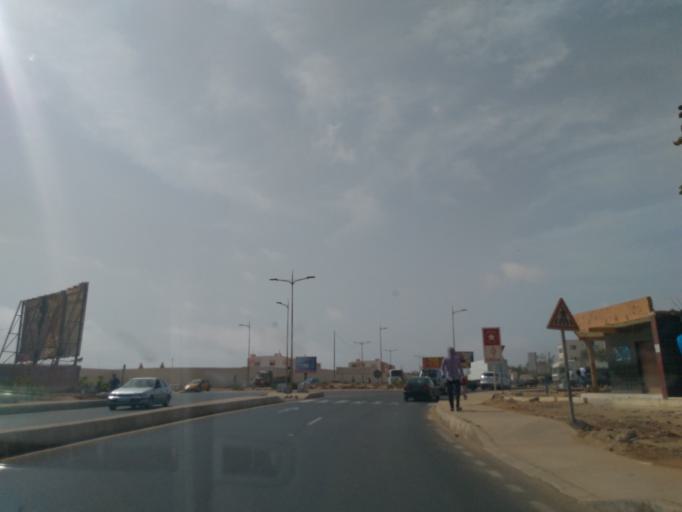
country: SN
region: Dakar
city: Mermoz Boabab
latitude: 14.7094
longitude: -17.4814
